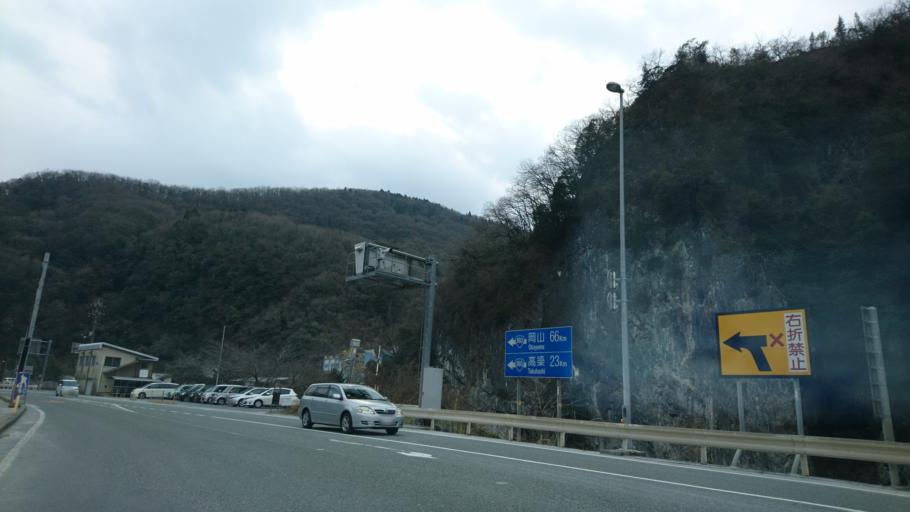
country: JP
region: Okayama
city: Niimi
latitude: 34.9234
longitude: 133.5200
